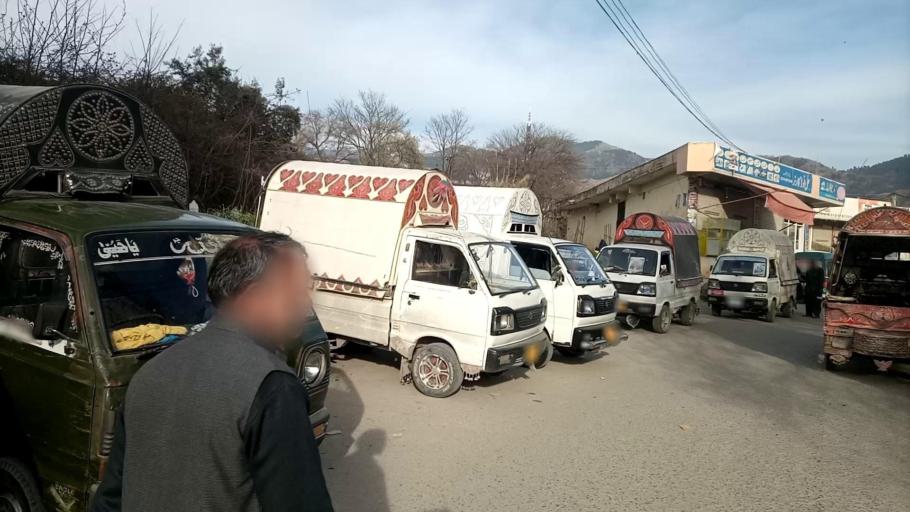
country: PK
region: Khyber Pakhtunkhwa
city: Abbottabad
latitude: 34.1673
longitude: 73.2639
